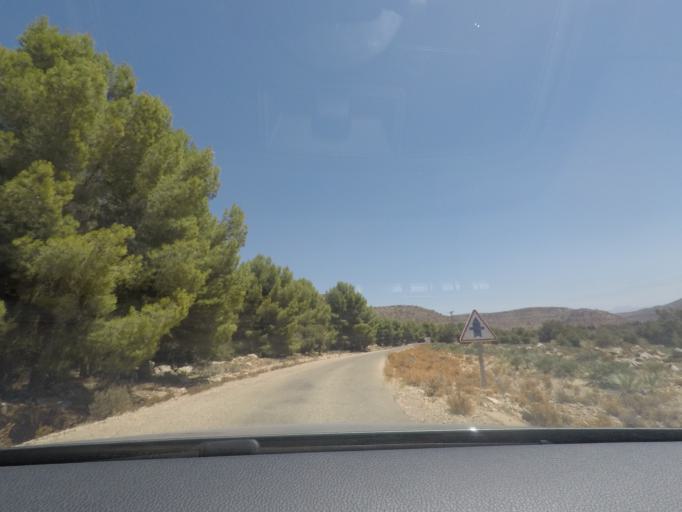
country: MA
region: Souss-Massa-Draa
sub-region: Agadir-Ida-ou-Tnan
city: Tadrart
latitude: 30.7460
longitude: -9.3587
